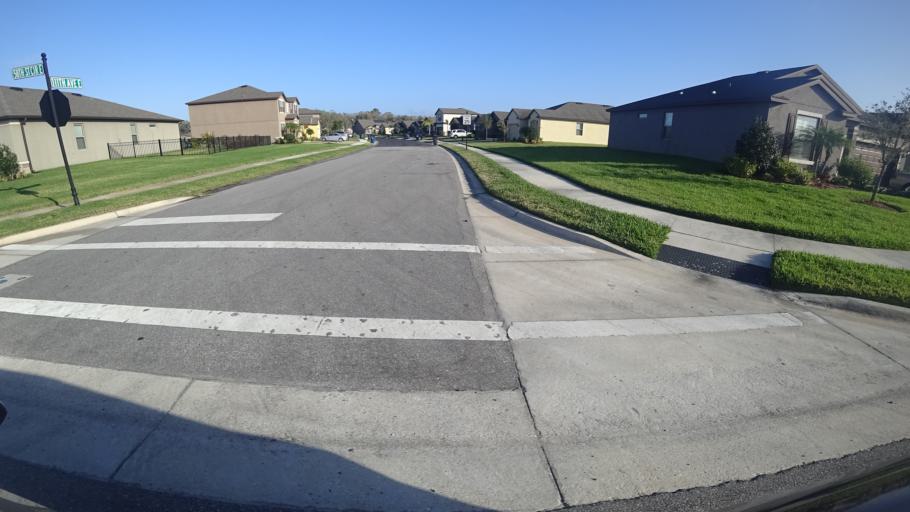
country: US
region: Florida
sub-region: Manatee County
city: Ellenton
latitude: 27.5686
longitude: -82.4499
